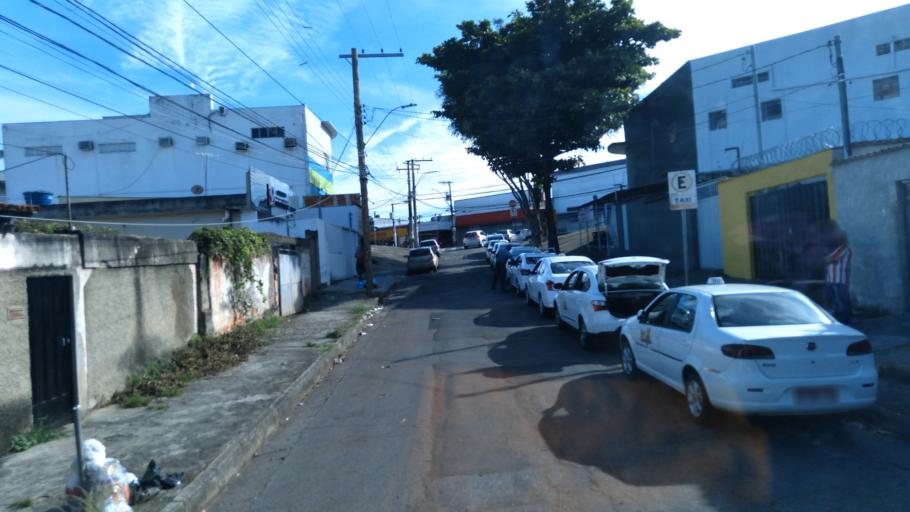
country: BR
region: Minas Gerais
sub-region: Contagem
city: Contagem
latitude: -19.9000
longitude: -44.0058
